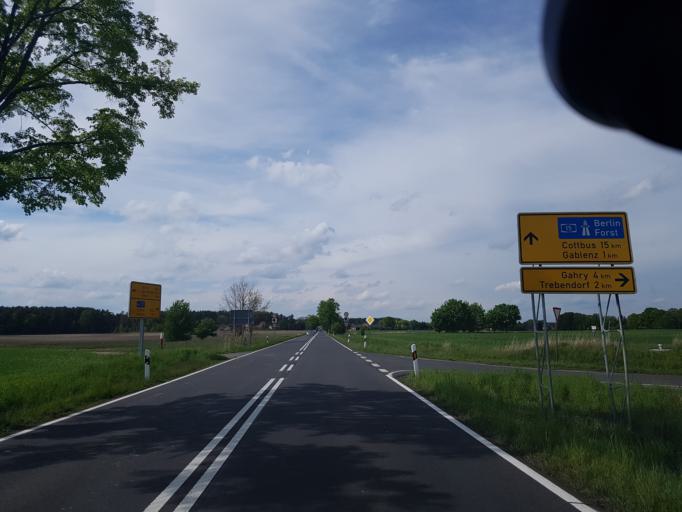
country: DE
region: Saxony
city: Gross Duben
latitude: 51.6795
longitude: 14.5124
